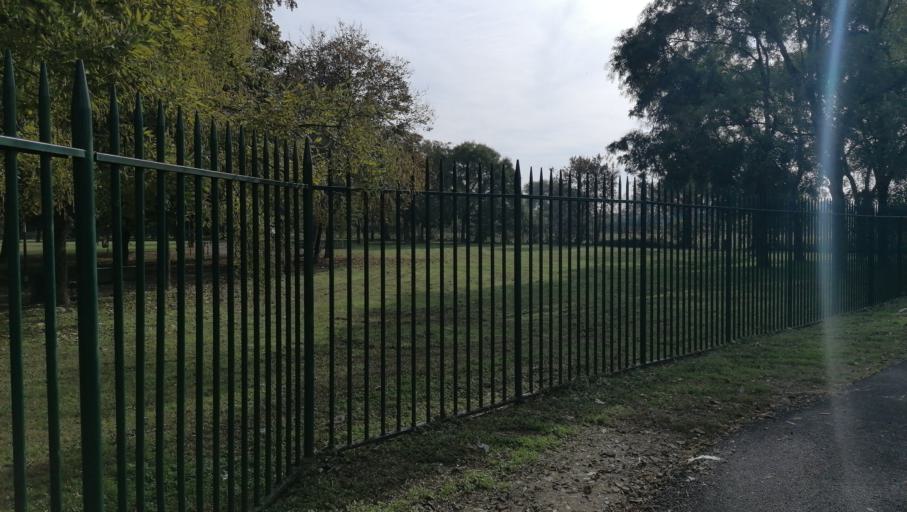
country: IT
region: Lombardy
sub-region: Citta metropolitana di Milano
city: Chiaravalle
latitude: 45.4353
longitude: 9.2149
